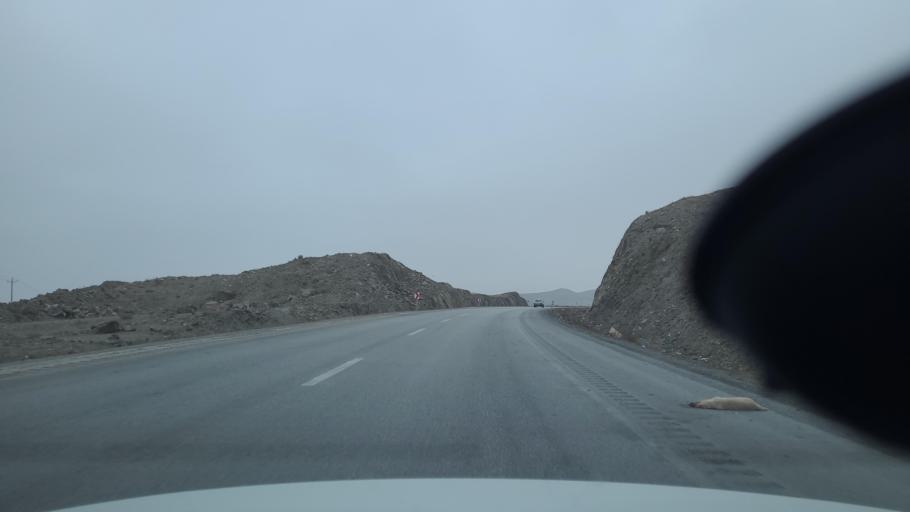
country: IR
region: Razavi Khorasan
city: Fariman
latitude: 35.9943
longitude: 59.7553
